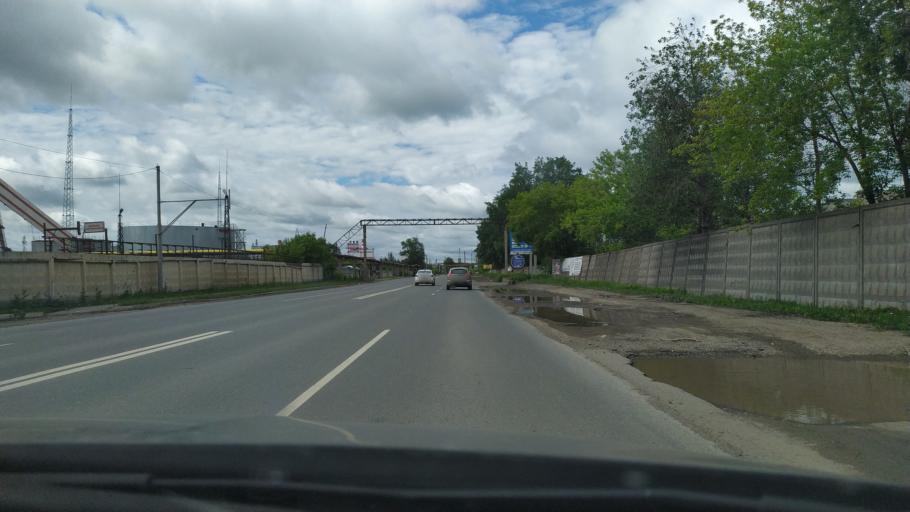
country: RU
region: Perm
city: Kondratovo
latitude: 57.9295
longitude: 56.1442
